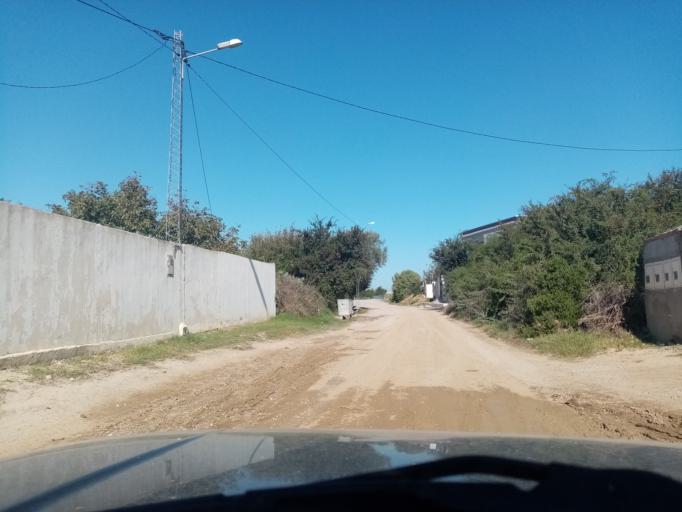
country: TN
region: Nabul
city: Bu `Urqub
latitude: 36.5785
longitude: 10.5709
